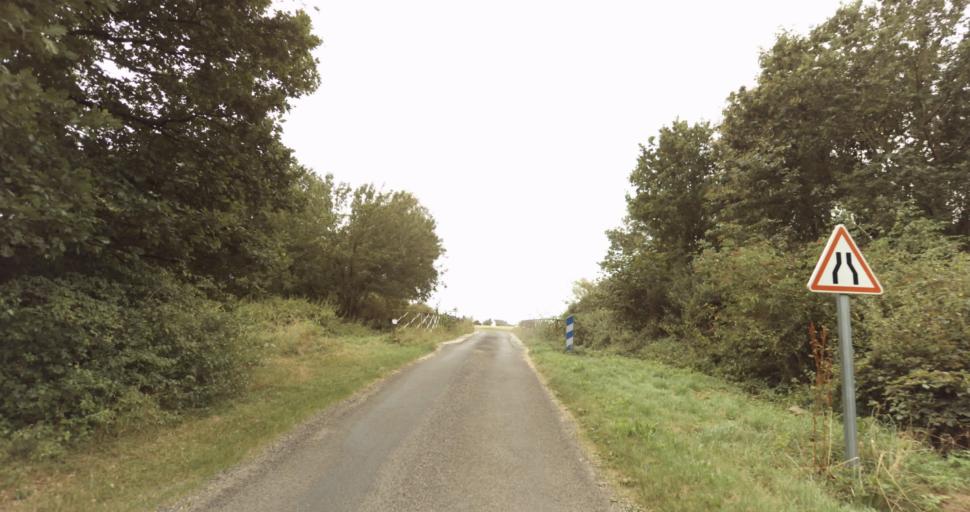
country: FR
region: Haute-Normandie
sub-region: Departement de l'Eure
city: Marcilly-sur-Eure
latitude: 48.8296
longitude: 1.3141
